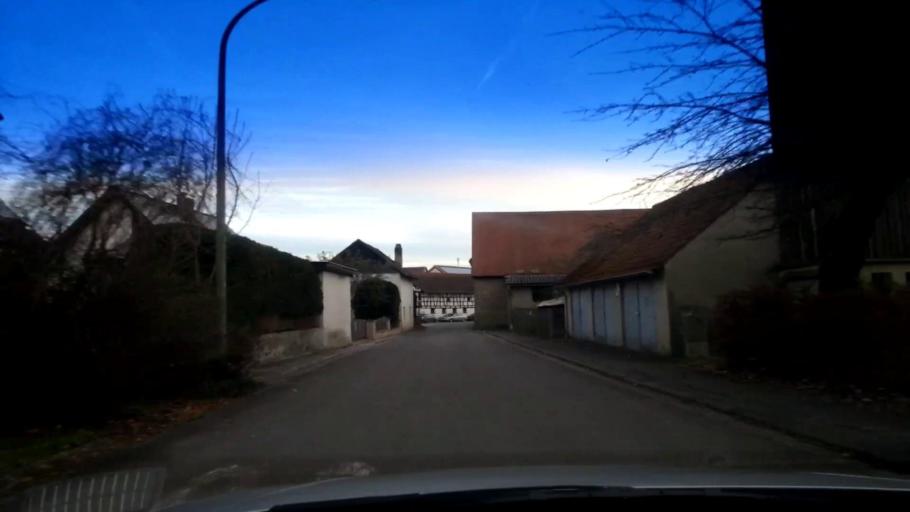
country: DE
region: Bavaria
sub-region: Upper Franconia
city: Strullendorf
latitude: 49.8676
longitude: 10.9961
